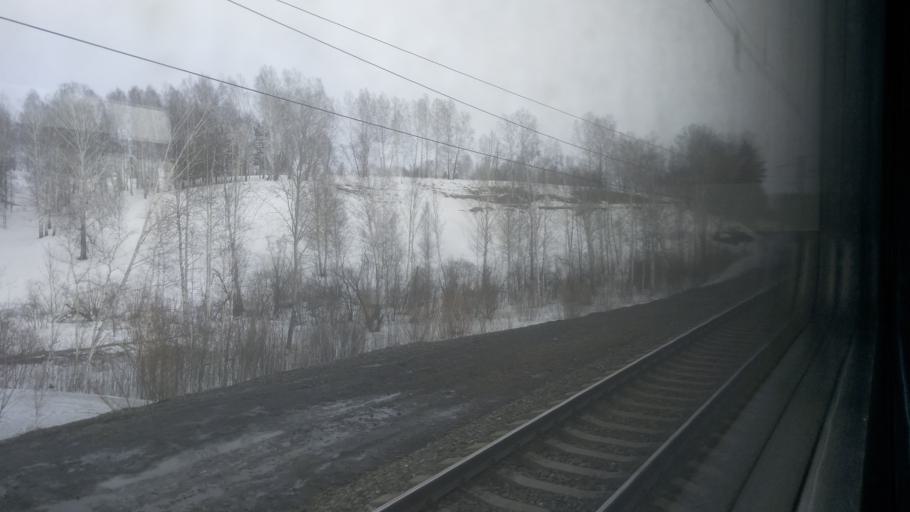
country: RU
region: Novosibirsk
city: Bolotnoye
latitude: 55.5971
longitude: 84.1425
